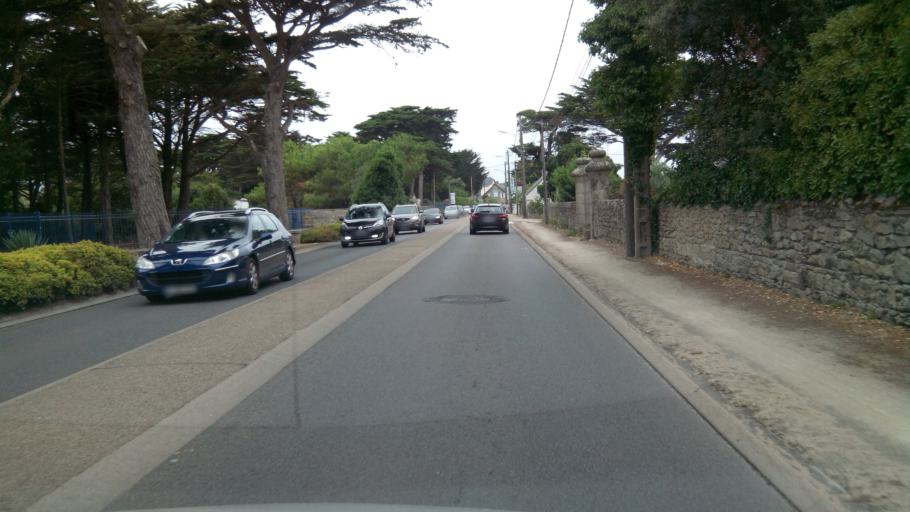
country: FR
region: Pays de la Loire
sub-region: Departement de la Loire-Atlantique
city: Le Croisic
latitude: 47.2817
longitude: -2.4990
